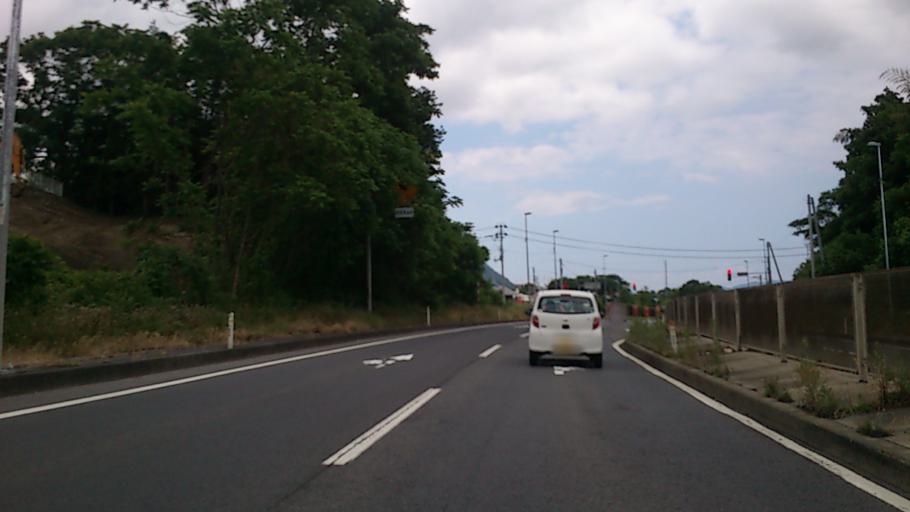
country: JP
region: Yamagata
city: Kaminoyama
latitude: 38.1802
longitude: 140.3100
